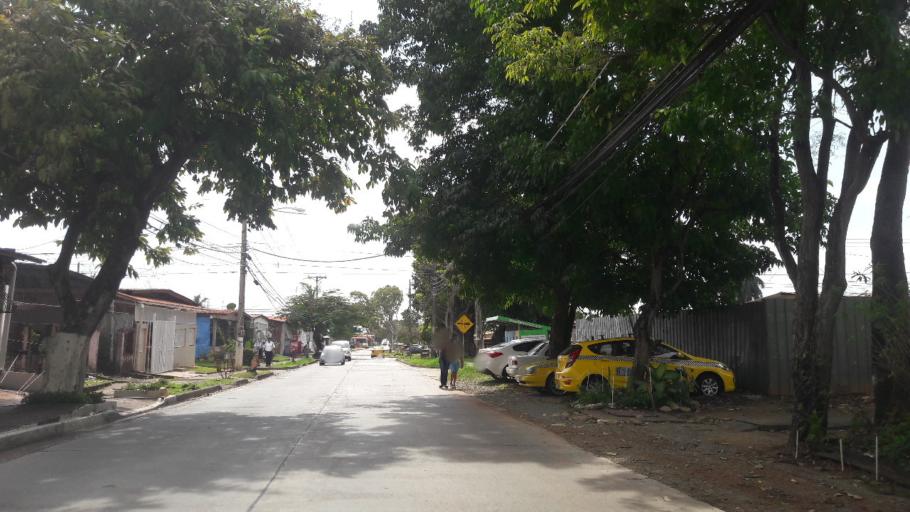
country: PA
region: Panama
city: Tocumen
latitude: 9.0598
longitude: -79.4199
